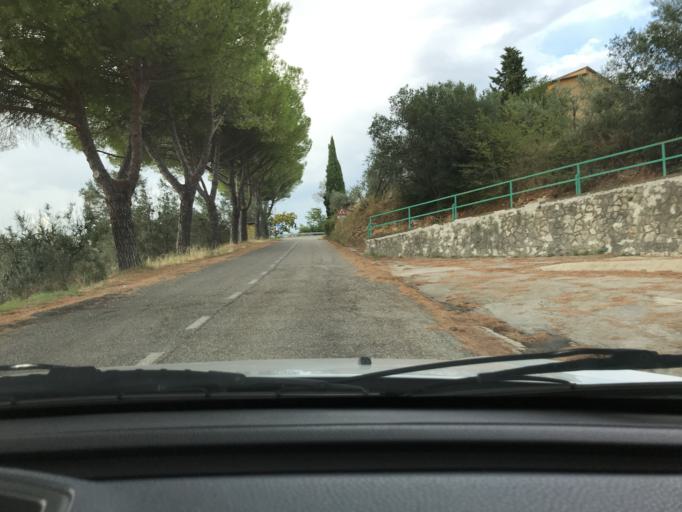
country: IT
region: Umbria
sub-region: Provincia di Terni
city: Montecchio
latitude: 42.6625
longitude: 12.2838
